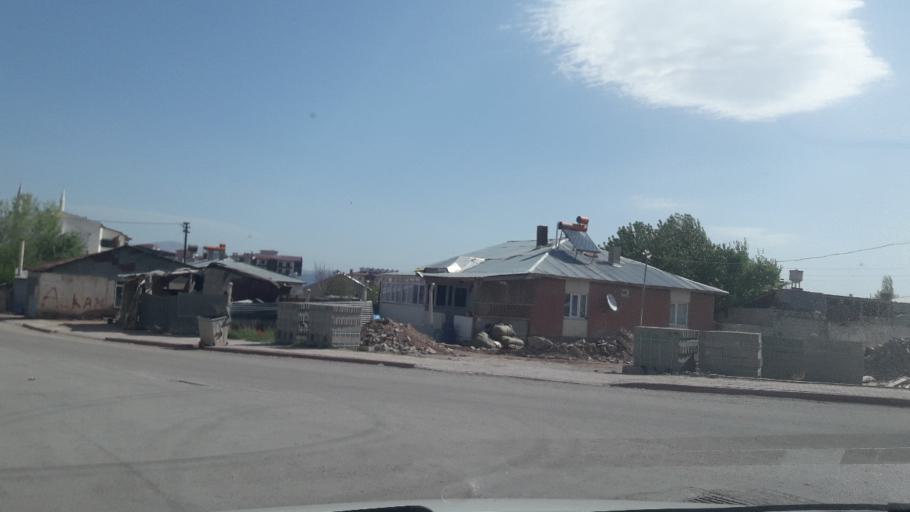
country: TR
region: Sivas
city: Kangal
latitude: 39.2295
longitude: 37.3885
